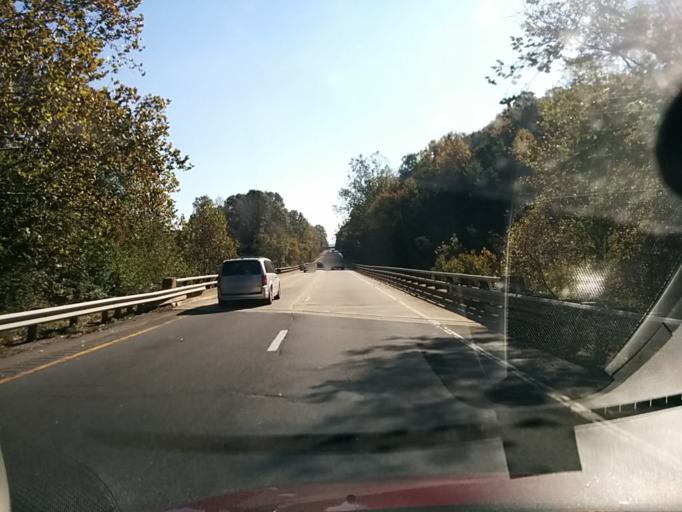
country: US
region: Virginia
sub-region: Albemarle County
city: Crozet
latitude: 38.0393
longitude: -78.7116
